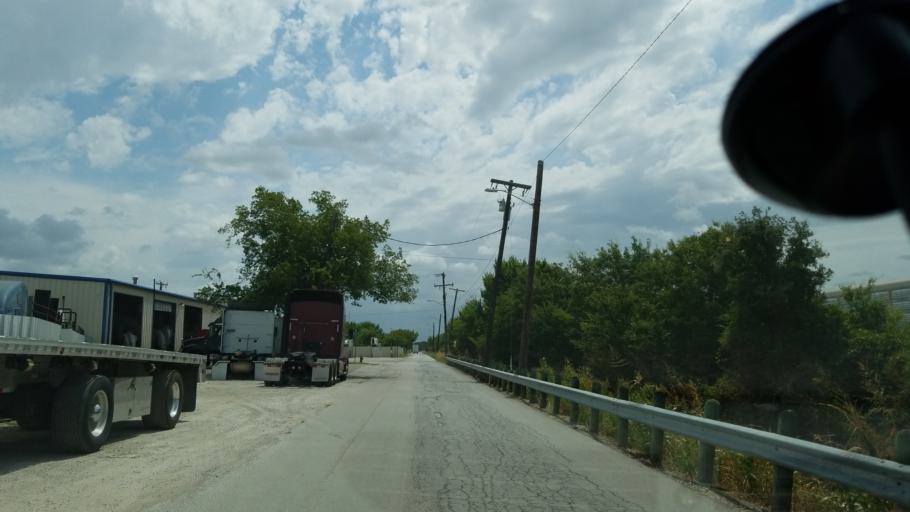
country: US
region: Texas
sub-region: Dallas County
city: Grand Prairie
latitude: 32.7462
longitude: -96.9780
